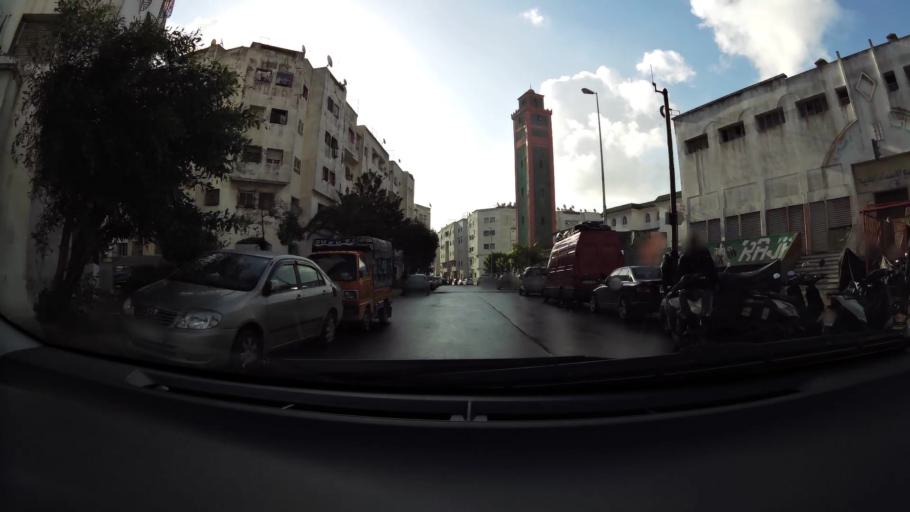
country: MA
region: Grand Casablanca
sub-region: Mediouna
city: Tit Mellil
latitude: 33.5994
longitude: -7.5226
